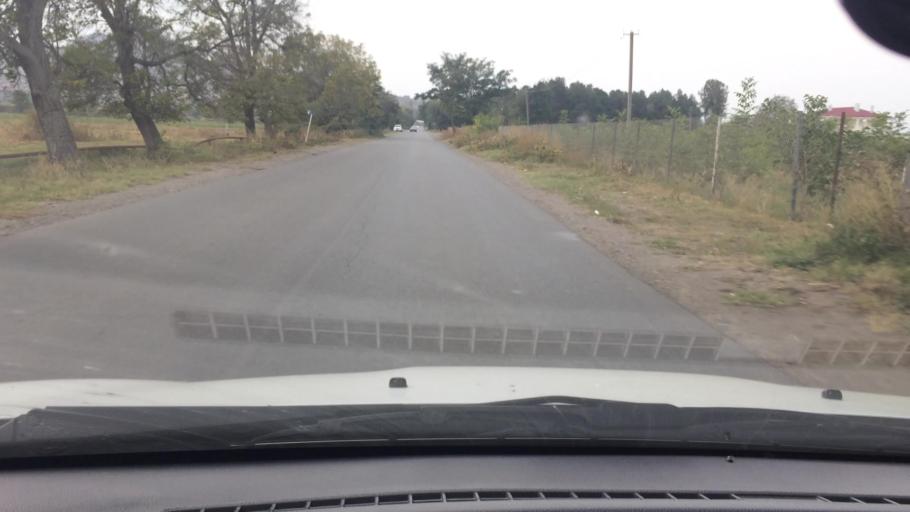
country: GE
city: Naghvarevi
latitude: 41.3566
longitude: 44.8550
